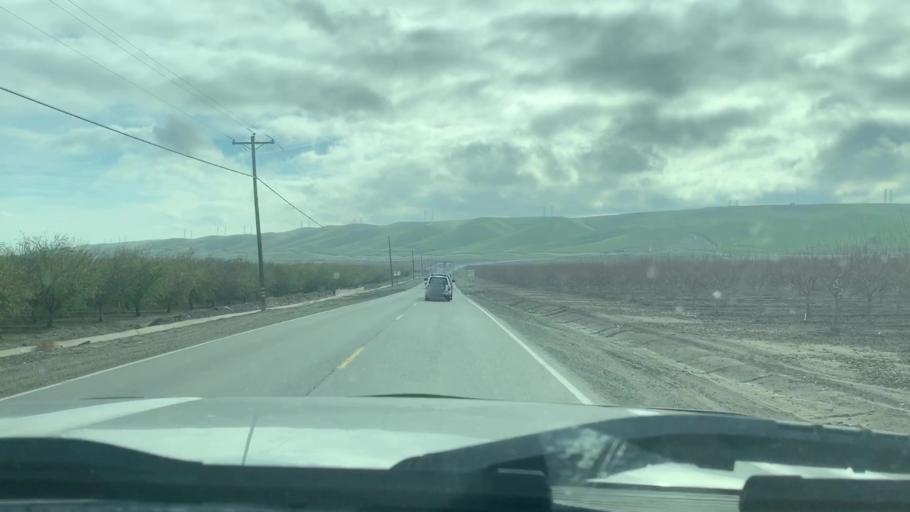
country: US
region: California
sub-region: Merced County
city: Los Banos
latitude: 36.9398
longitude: -120.8379
